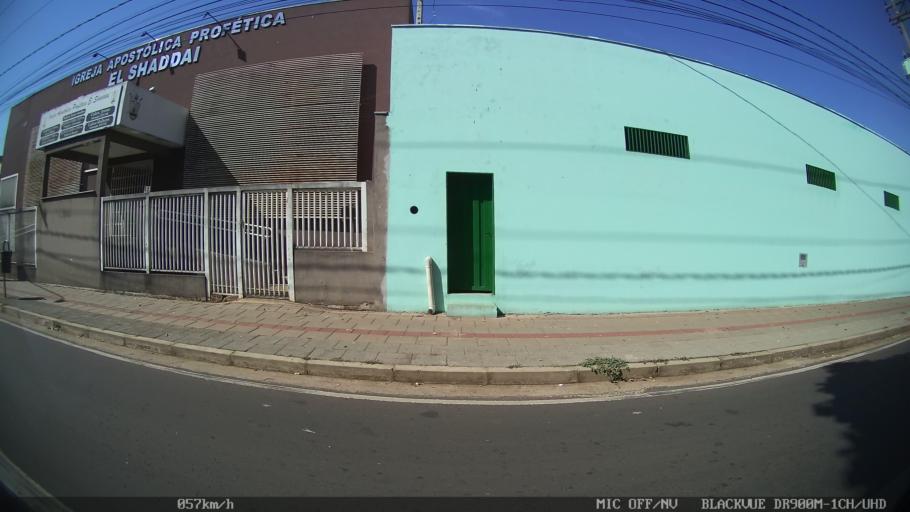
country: BR
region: Sao Paulo
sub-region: Sao Jose Do Rio Preto
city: Sao Jose do Rio Preto
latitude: -20.7935
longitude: -49.3888
